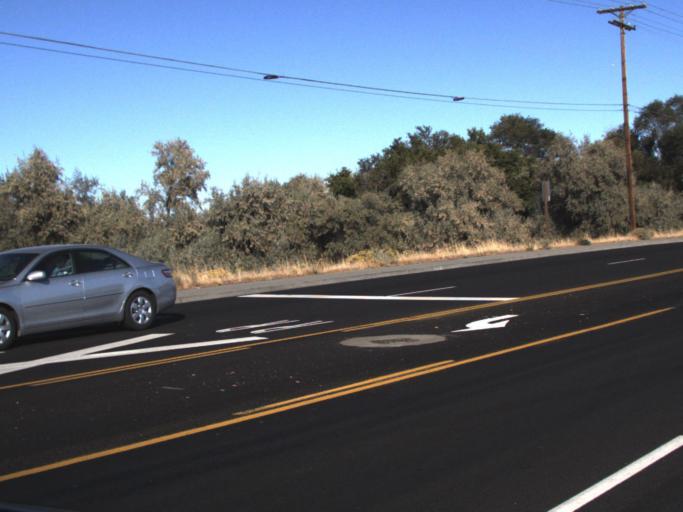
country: US
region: Washington
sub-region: Franklin County
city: Pasco
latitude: 46.2053
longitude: -119.1033
